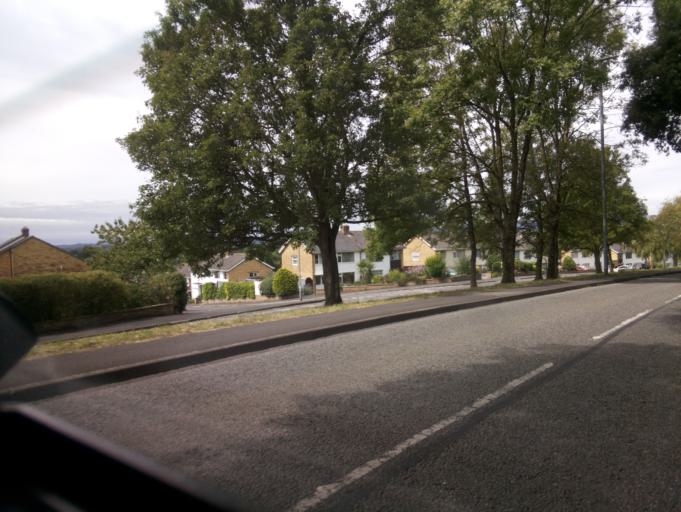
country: GB
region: England
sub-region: Somerset
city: Glastonbury
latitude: 51.1552
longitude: -2.7142
